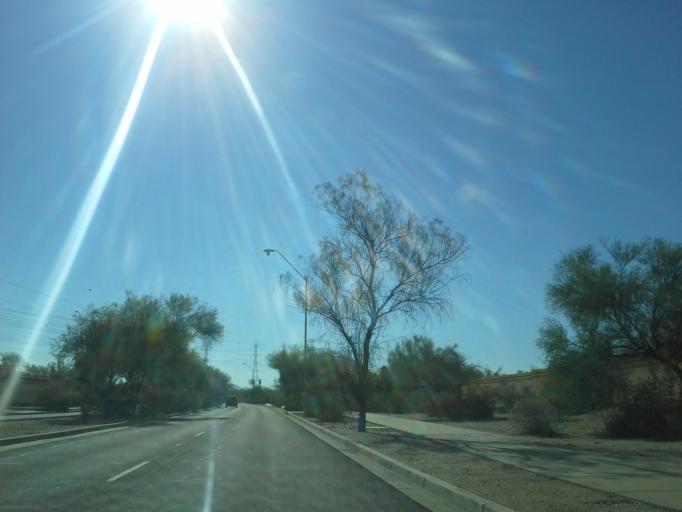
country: US
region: Arizona
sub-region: Maricopa County
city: Scottsdale
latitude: 33.6006
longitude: -111.8487
